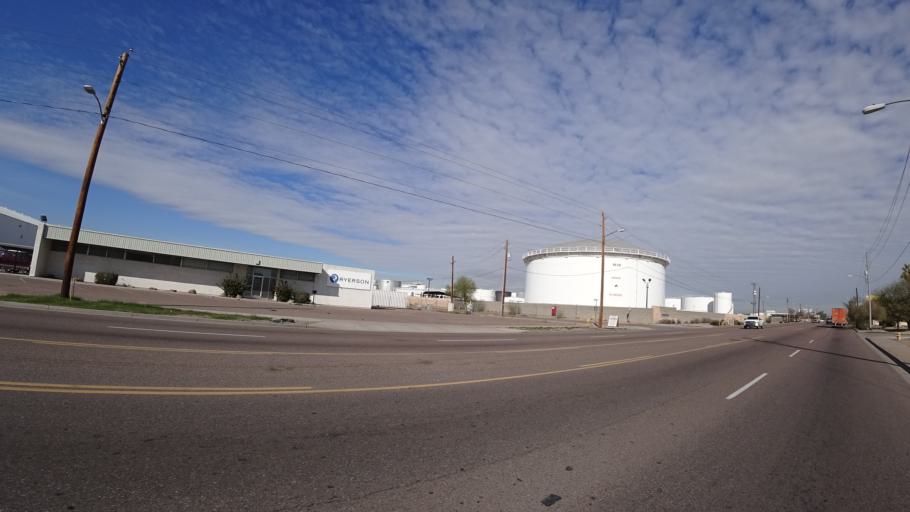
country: US
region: Arizona
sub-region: Maricopa County
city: Laveen
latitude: 33.4459
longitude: -112.1691
